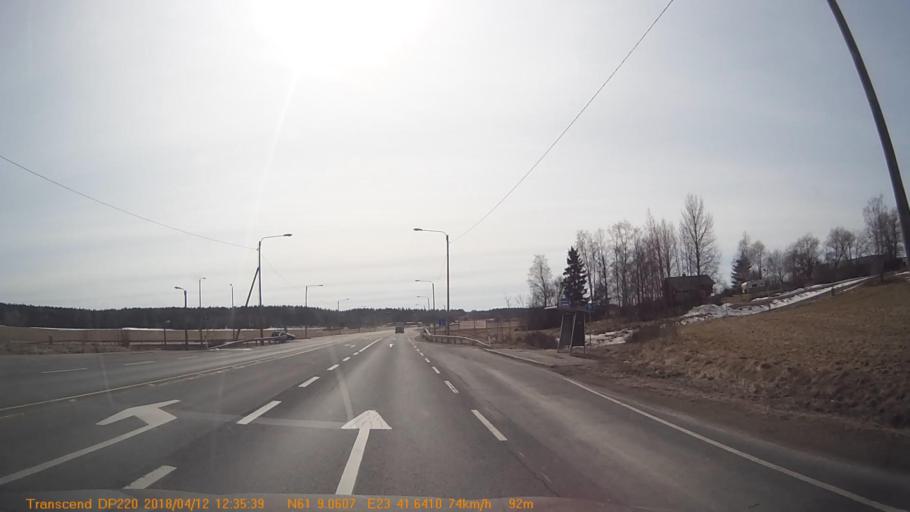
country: FI
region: Pirkanmaa
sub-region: Etelae-Pirkanmaa
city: Kylmaekoski
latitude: 61.1510
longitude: 23.6940
